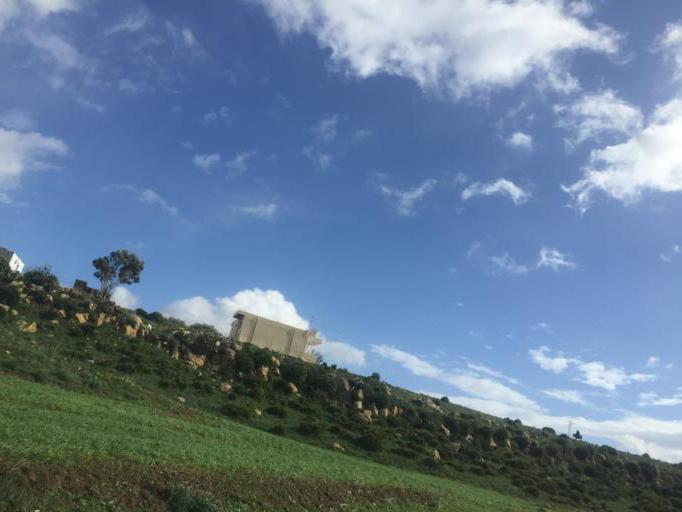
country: TN
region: Nabul
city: El Mida
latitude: 36.8103
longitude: 10.8452
